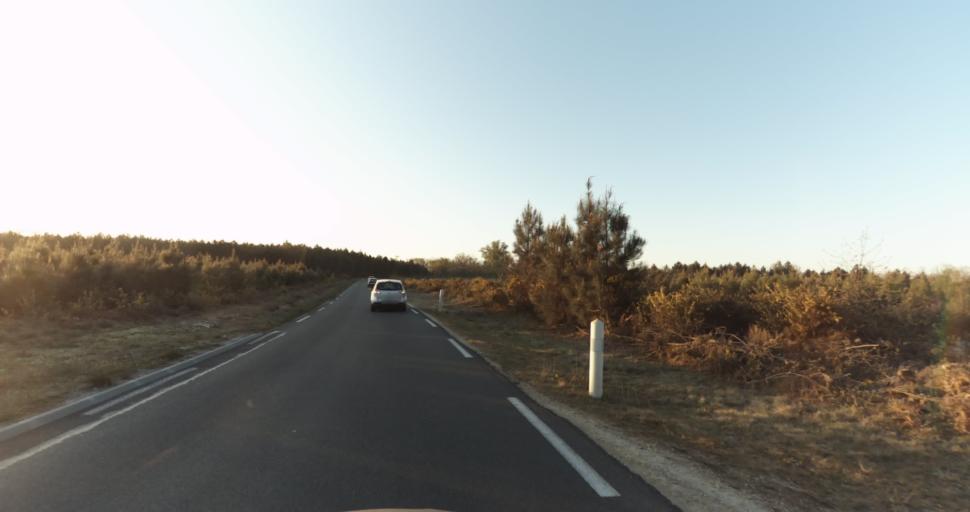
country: FR
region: Aquitaine
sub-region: Departement de la Gironde
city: Martignas-sur-Jalle
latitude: 44.8210
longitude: -0.7561
